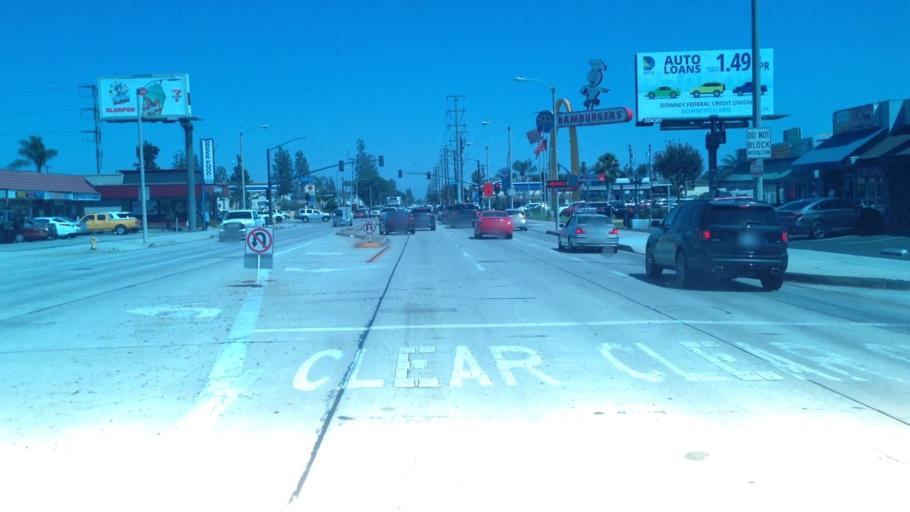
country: US
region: California
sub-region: Los Angeles County
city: Downey
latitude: 33.9482
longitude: -118.1186
